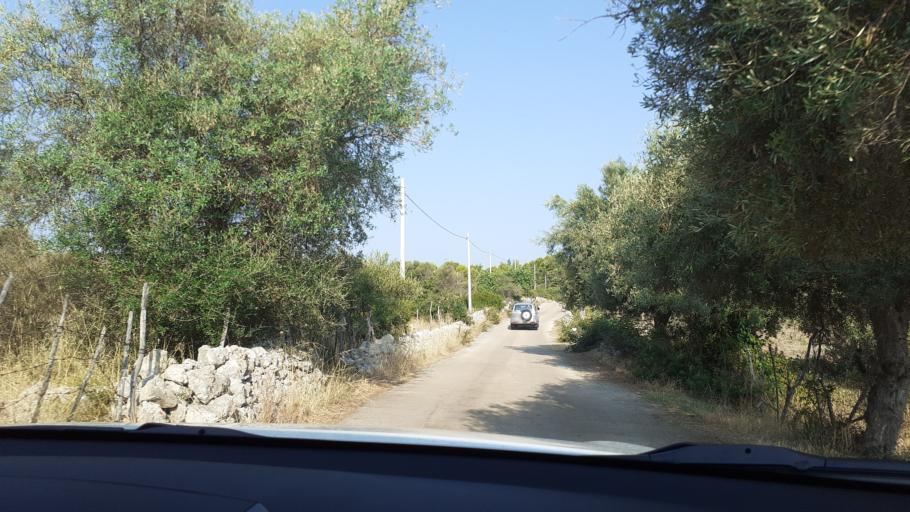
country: IT
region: Sicily
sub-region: Provincia di Siracusa
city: Cassibile
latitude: 36.9773
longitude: 15.1537
